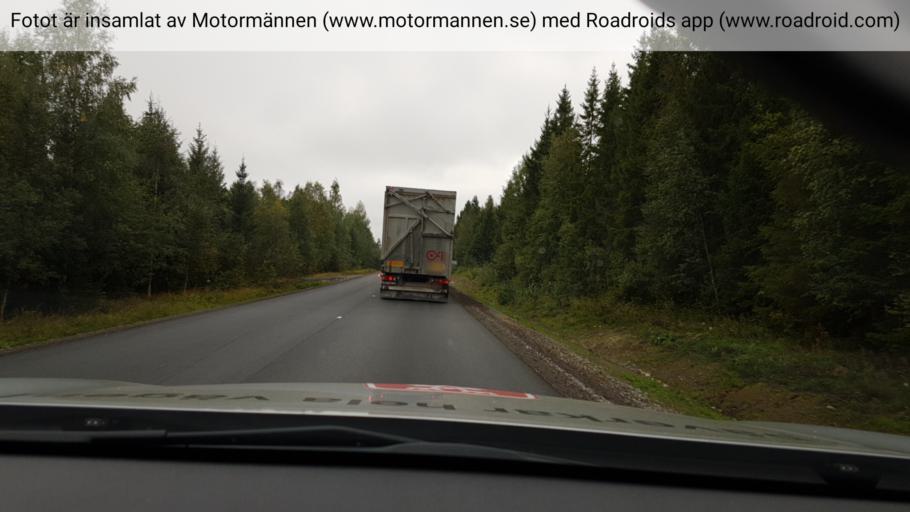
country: SE
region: Vaesterbotten
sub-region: Skelleftea Kommun
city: Burtraesk
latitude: 64.3789
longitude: 20.5118
